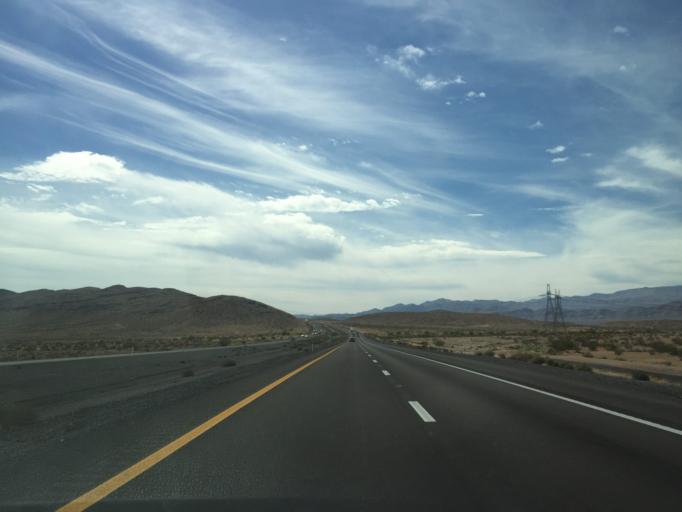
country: US
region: Nevada
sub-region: Clark County
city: Moapa Town
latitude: 36.4752
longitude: -114.8155
